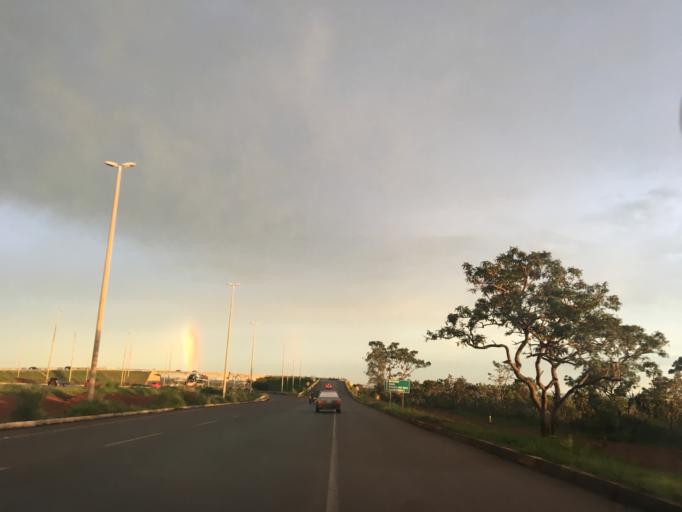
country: BR
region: Federal District
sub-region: Brasilia
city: Brasilia
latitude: -15.9756
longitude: -47.9896
